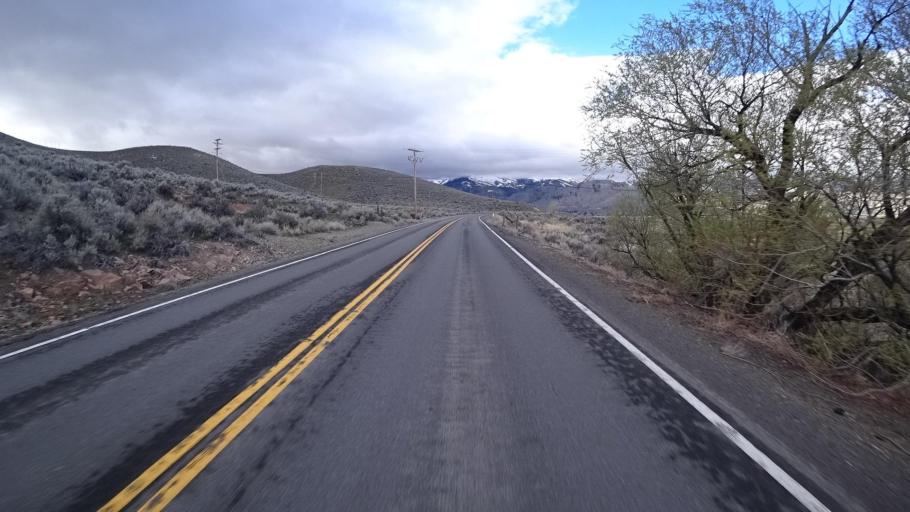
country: US
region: Nevada
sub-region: Carson City
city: Carson City
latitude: 39.2298
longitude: -119.7843
